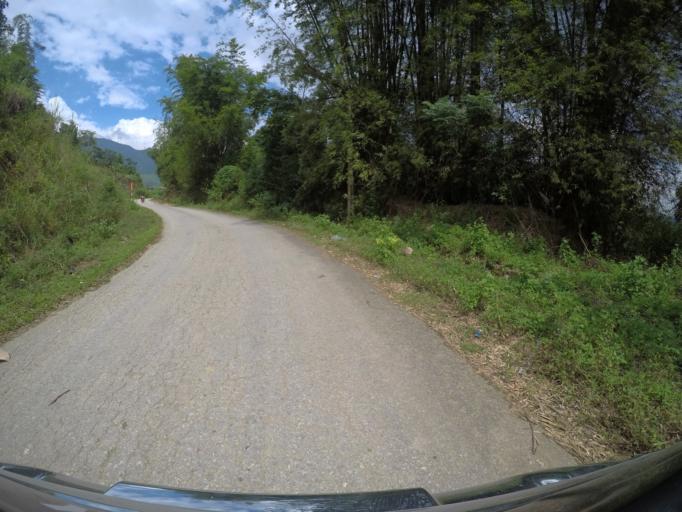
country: VN
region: Yen Bai
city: Son Thinh
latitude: 21.6560
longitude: 104.5003
